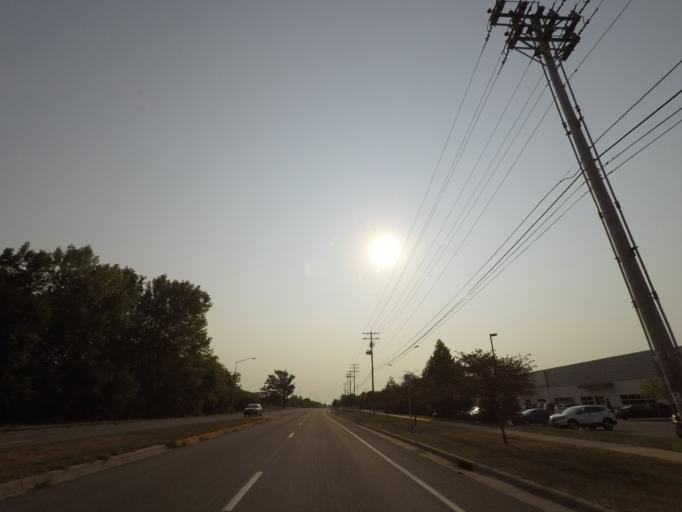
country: US
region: Wisconsin
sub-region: Dane County
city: McFarland
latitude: 43.0517
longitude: -89.2900
